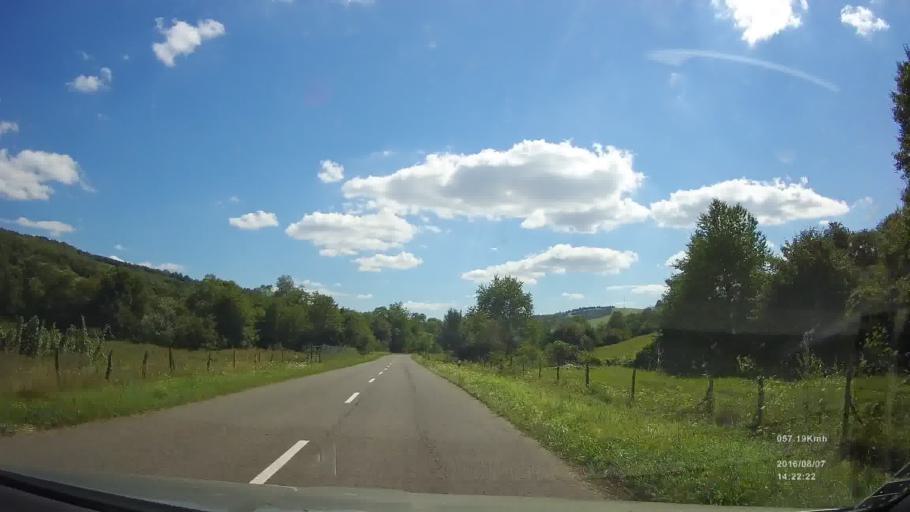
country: SK
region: Presovsky
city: Stropkov
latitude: 49.2746
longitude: 21.7517
